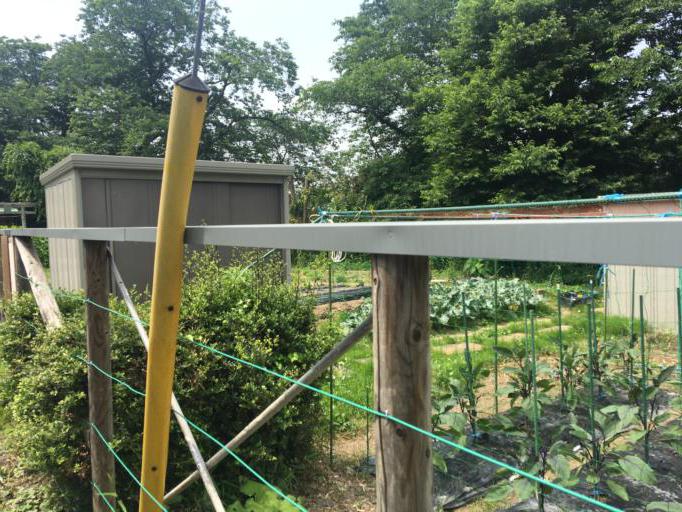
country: JP
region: Saitama
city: Koshigaya
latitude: 35.8972
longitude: 139.7880
